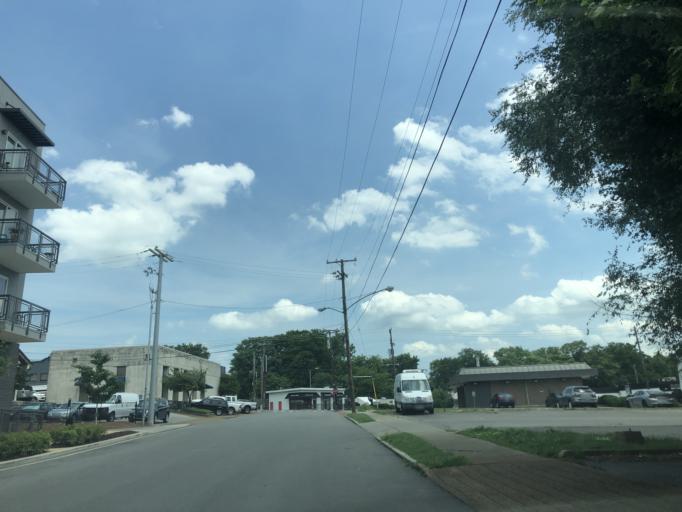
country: US
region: Tennessee
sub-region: Davidson County
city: Nashville
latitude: 36.1823
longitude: -86.7502
